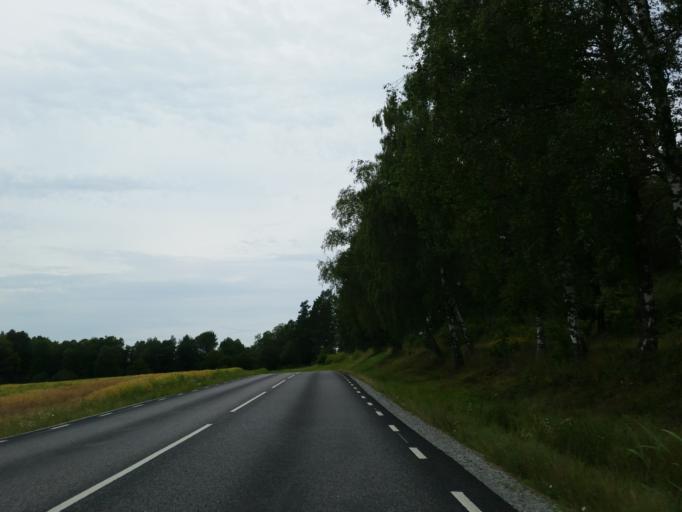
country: SE
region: Stockholm
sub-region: Salems Kommun
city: Ronninge
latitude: 59.2289
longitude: 17.7216
